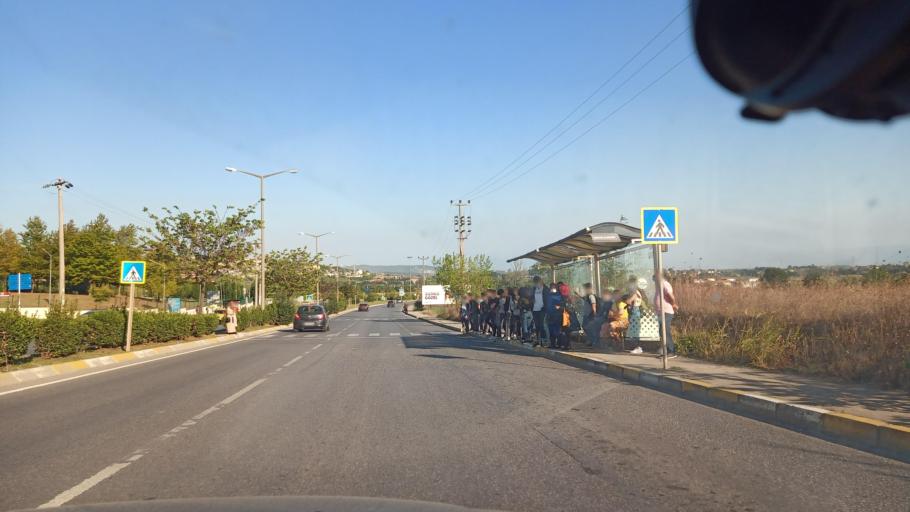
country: TR
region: Sakarya
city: Kazimpasa
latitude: 40.8515
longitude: 30.3135
